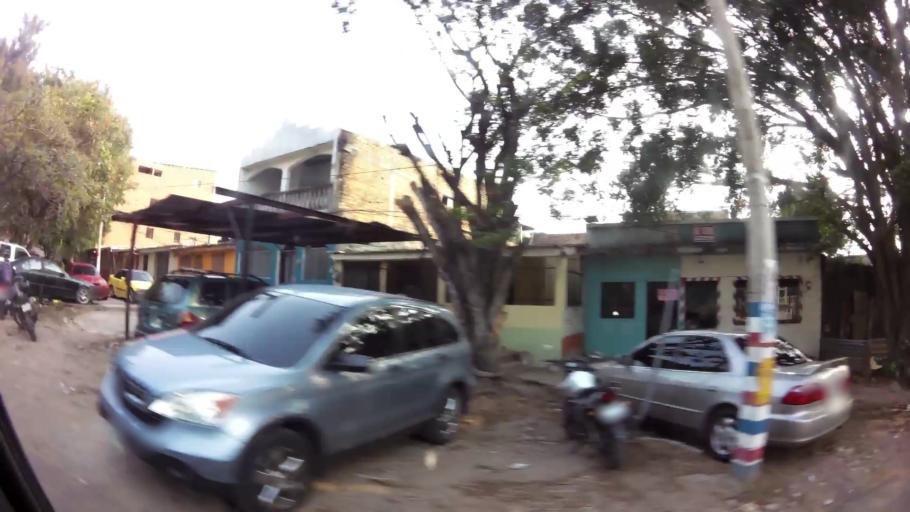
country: HN
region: Francisco Morazan
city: Tegucigalpa
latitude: 14.0682
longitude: -87.1771
